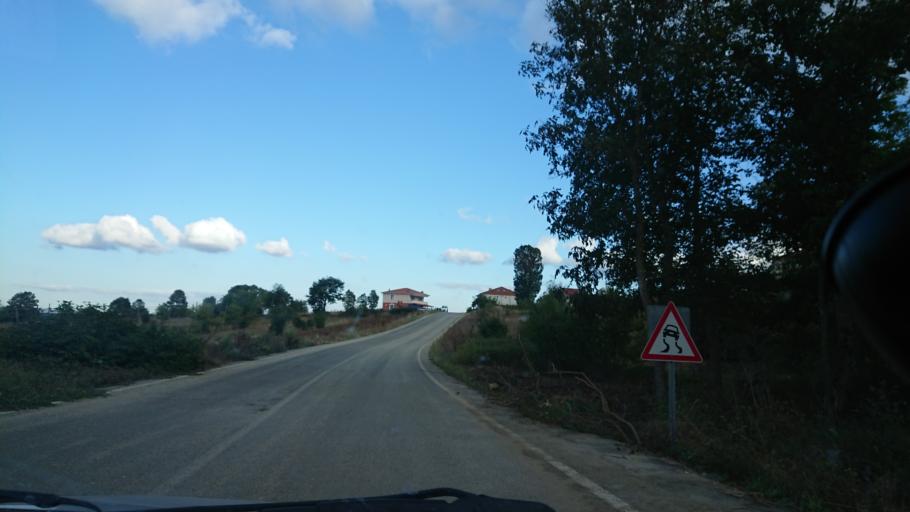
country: TR
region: Bilecik
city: Pazaryeri
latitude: 40.0107
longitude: 29.8025
